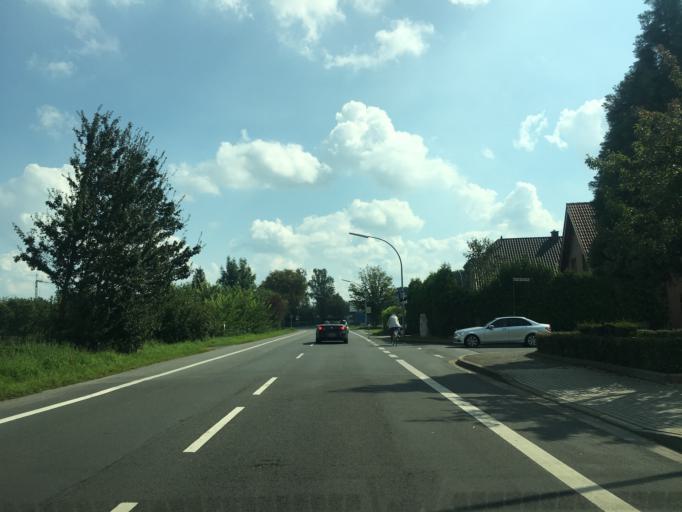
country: DE
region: North Rhine-Westphalia
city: Selm
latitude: 51.6955
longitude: 7.4785
